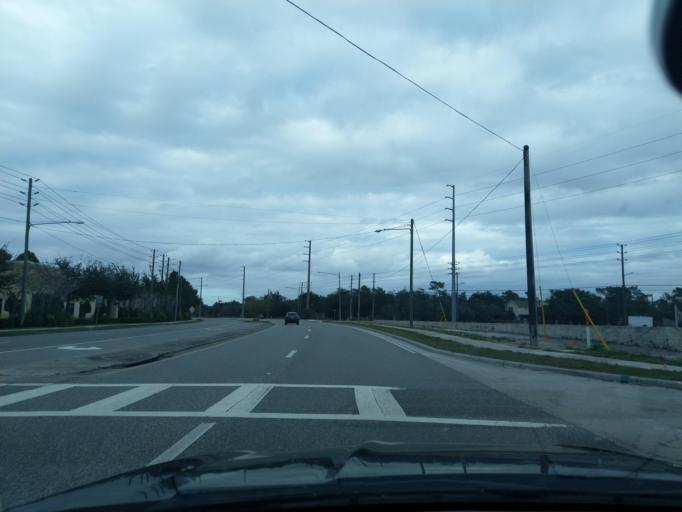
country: US
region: Florida
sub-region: Orange County
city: Doctor Phillips
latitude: 28.3982
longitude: -81.5037
